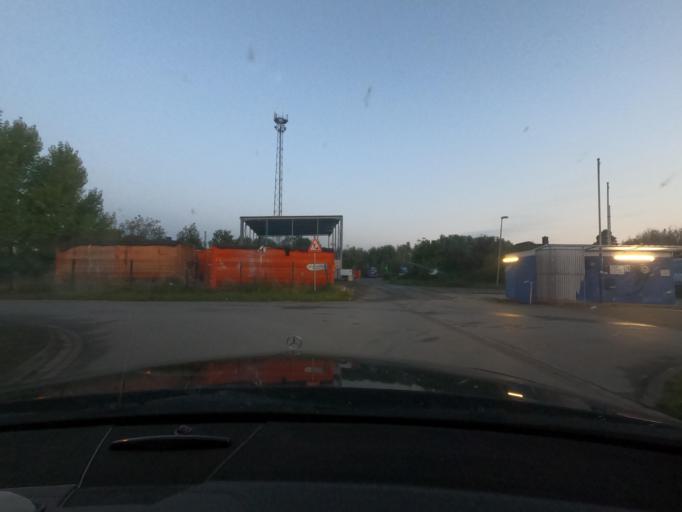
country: DE
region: North Rhine-Westphalia
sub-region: Regierungsbezirk Detmold
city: Salzkotten
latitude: 51.6679
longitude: 8.5917
